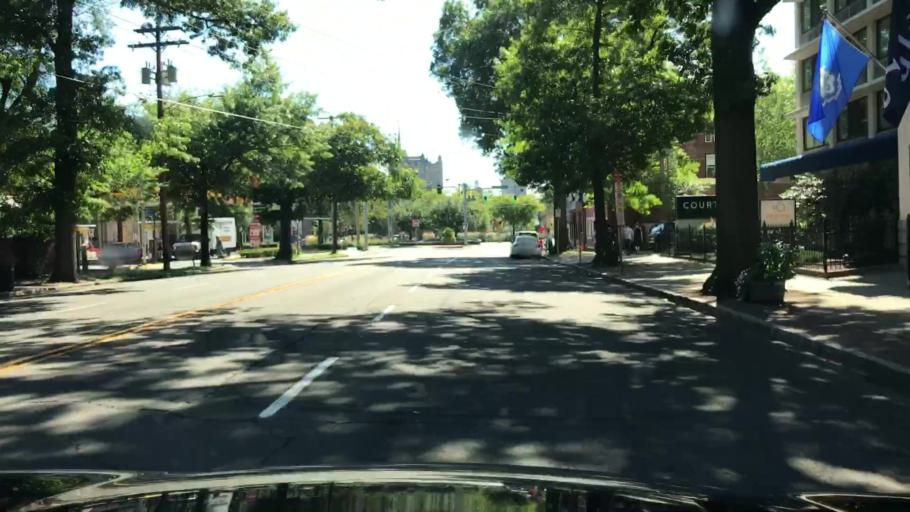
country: US
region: Connecticut
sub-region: New Haven County
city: New Haven
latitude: 41.3133
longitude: -72.9338
